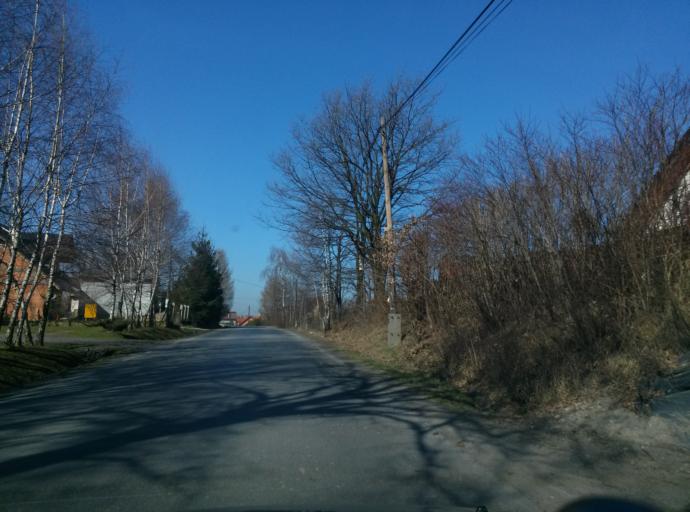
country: PL
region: Lesser Poland Voivodeship
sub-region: Powiat krakowski
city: Mogilany
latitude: 49.9451
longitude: 19.8622
